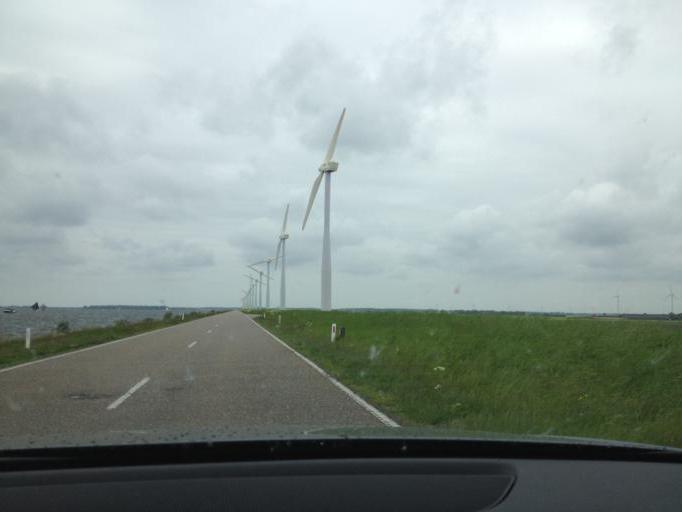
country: NL
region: Utrecht
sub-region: Gemeente Bunschoten
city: Spakenburg
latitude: 52.2710
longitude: 5.3740
